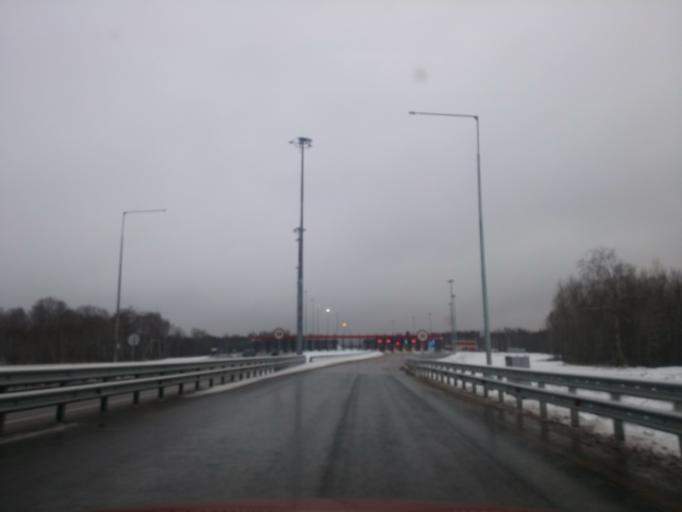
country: RU
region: Tverskaya
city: Likhoslavl'
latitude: 56.9580
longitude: 35.5019
